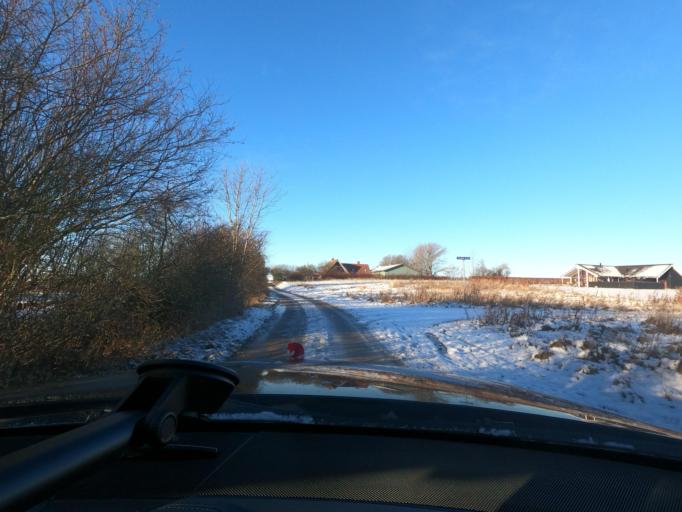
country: DK
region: South Denmark
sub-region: Sonderborg Kommune
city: Horuphav
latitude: 54.8717
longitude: 9.8880
